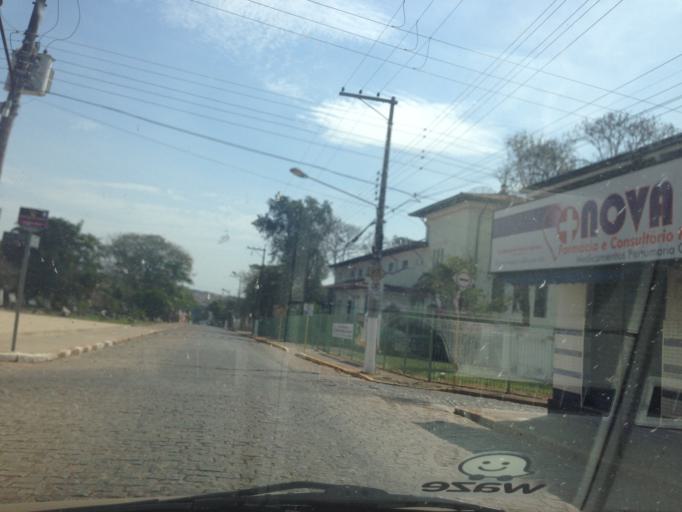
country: BR
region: Sao Paulo
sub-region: Casa Branca
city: Casa Branca
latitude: -21.7711
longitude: -47.0877
